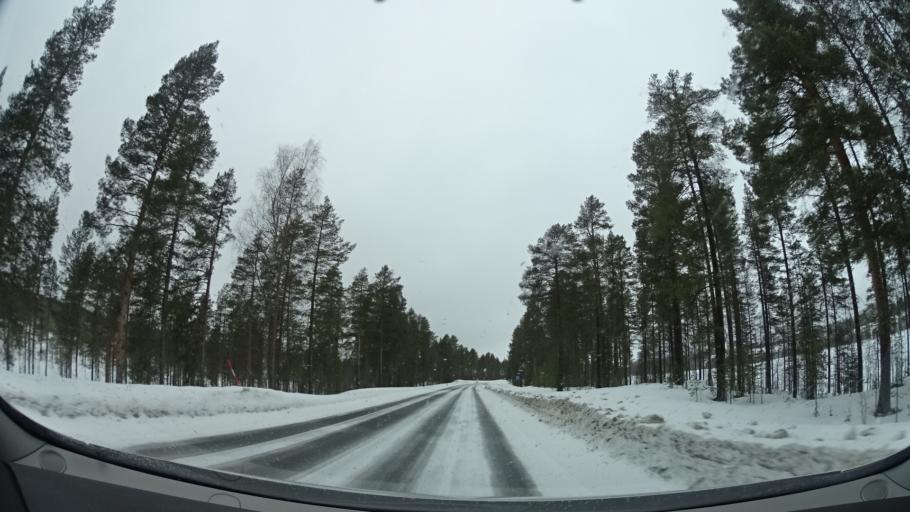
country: SE
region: Vaesterbotten
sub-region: Mala Kommun
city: Mala
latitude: 65.1499
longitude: 18.8111
